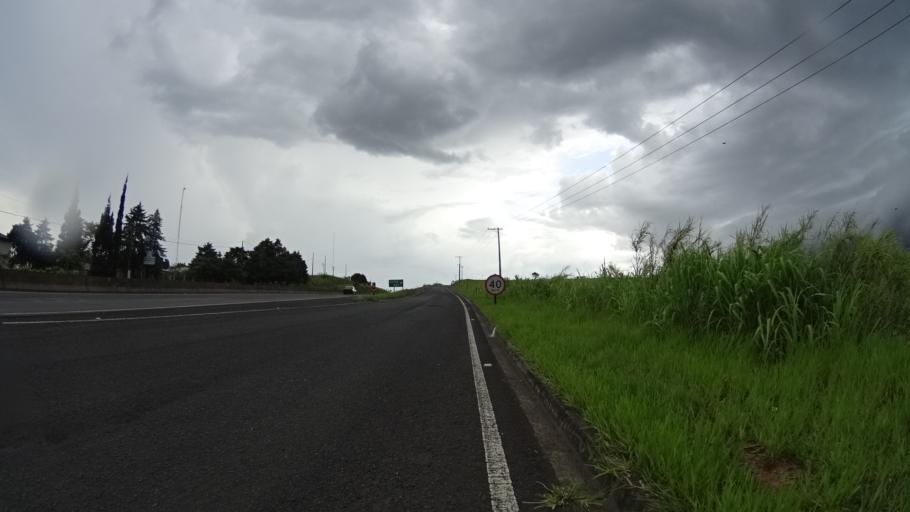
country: BR
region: Sao Paulo
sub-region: Marilia
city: Marilia
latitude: -22.2215
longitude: -49.8763
